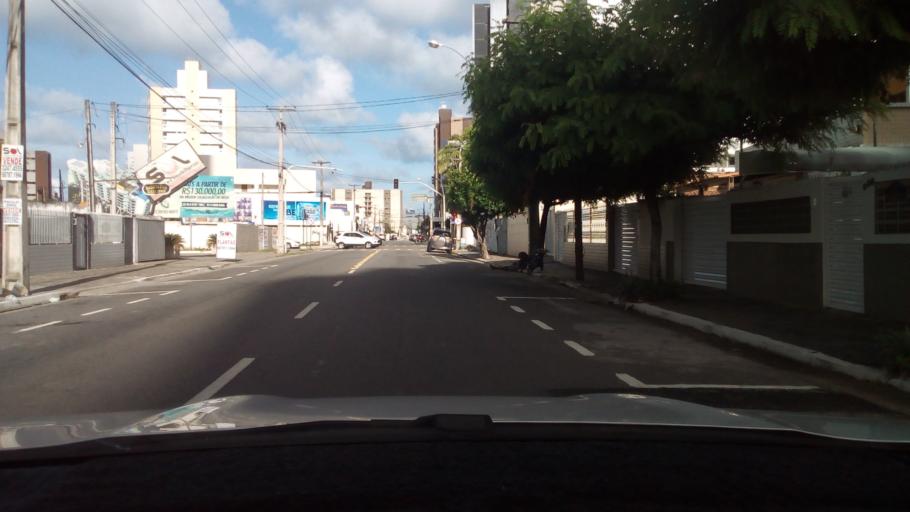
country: BR
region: Paraiba
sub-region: Joao Pessoa
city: Joao Pessoa
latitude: -7.1138
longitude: -34.8289
